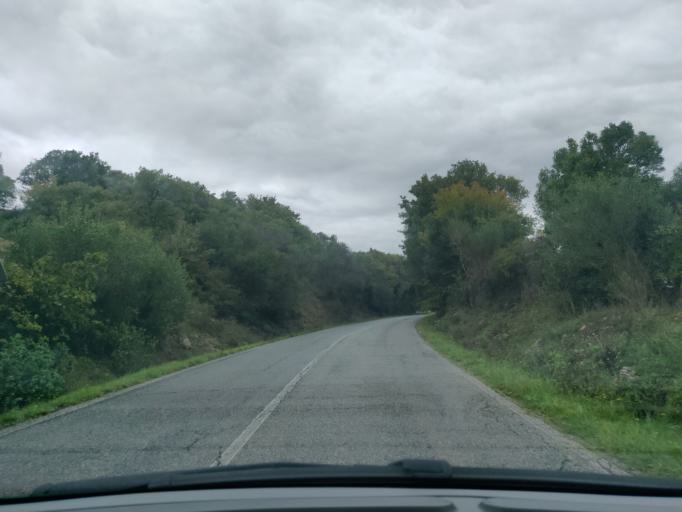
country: IT
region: Latium
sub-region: Citta metropolitana di Roma Capitale
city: Allumiere
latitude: 42.1343
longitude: 11.8698
